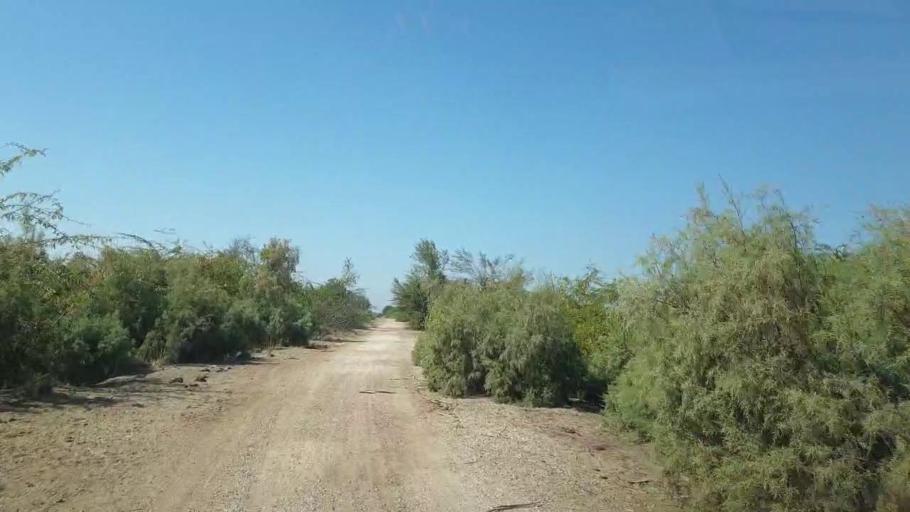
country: PK
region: Sindh
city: Mirpur Khas
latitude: 25.6162
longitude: 69.1346
